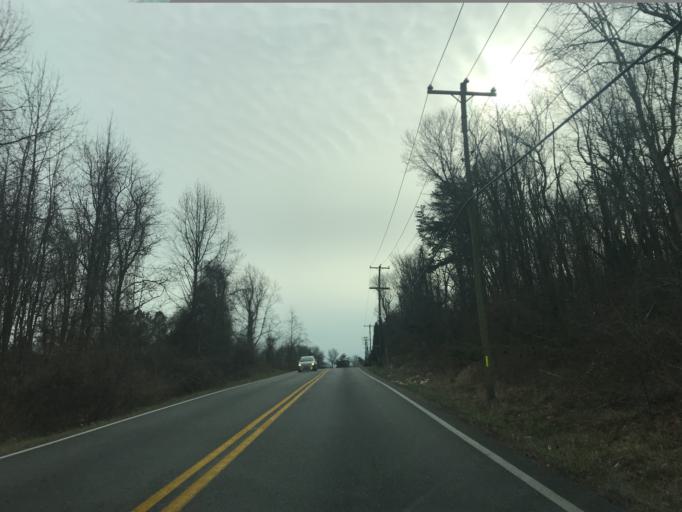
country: US
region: Maryland
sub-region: Cecil County
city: Elkton
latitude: 39.6151
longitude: -75.7919
